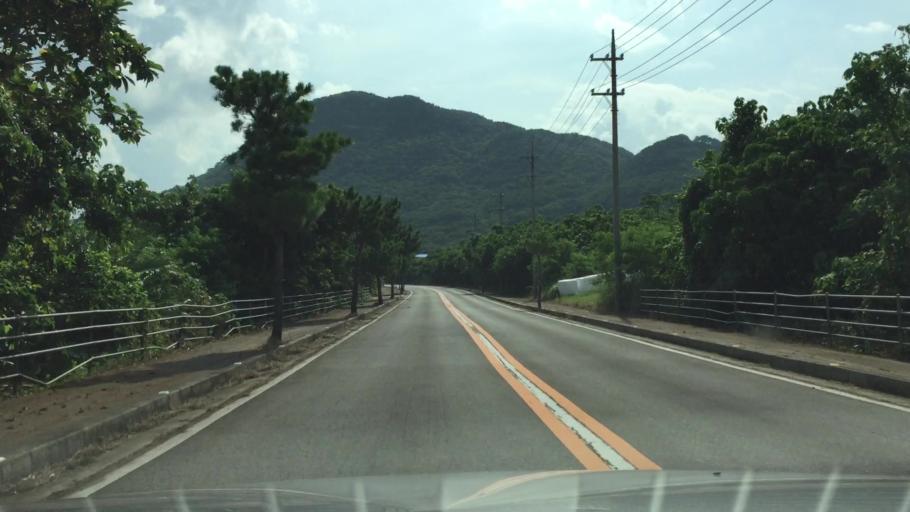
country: JP
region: Okinawa
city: Ishigaki
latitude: 24.4890
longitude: 124.2771
